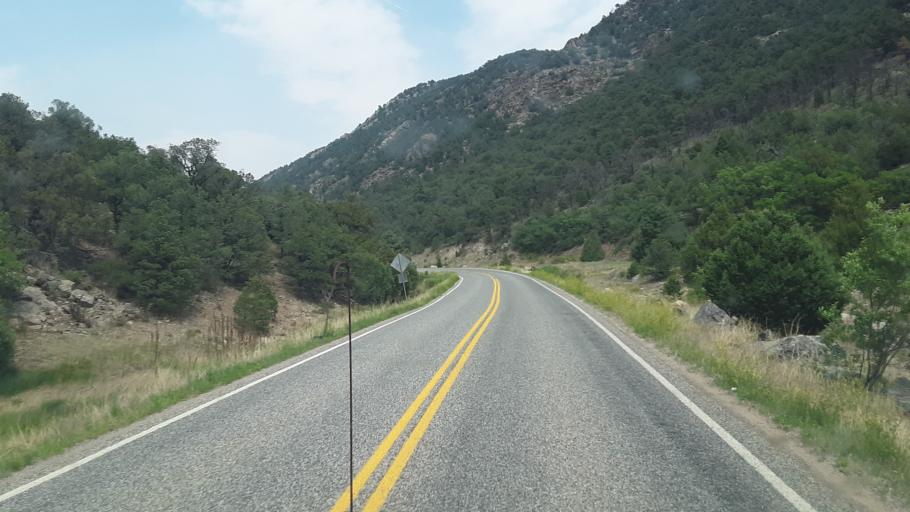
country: US
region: Colorado
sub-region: Fremont County
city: Canon City
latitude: 38.3976
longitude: -105.4459
